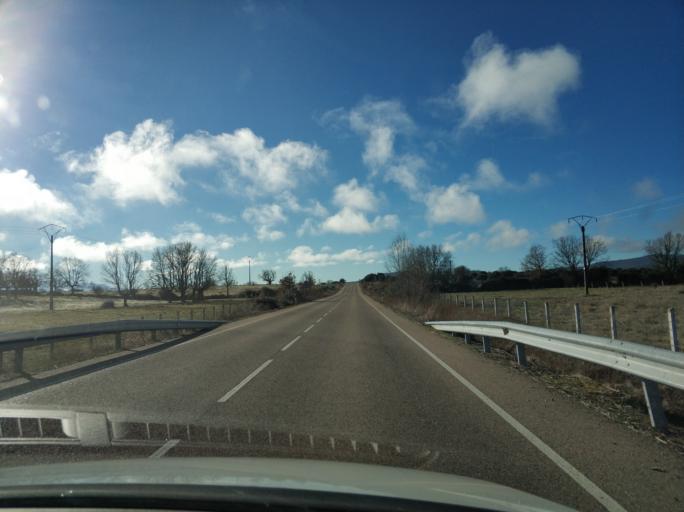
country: ES
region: Castille and Leon
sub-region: Provincia de Salamanca
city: Herguijuela del Campo
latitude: 40.6377
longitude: -5.9038
